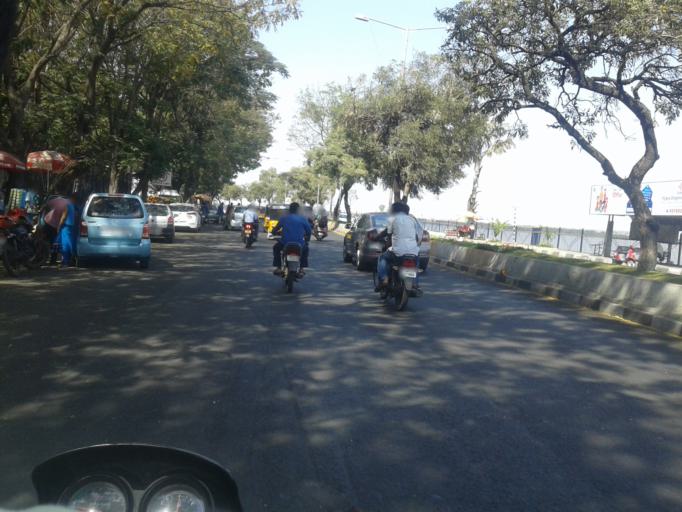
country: IN
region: Telangana
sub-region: Hyderabad
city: Hyderabad
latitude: 17.4125
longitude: 78.4710
